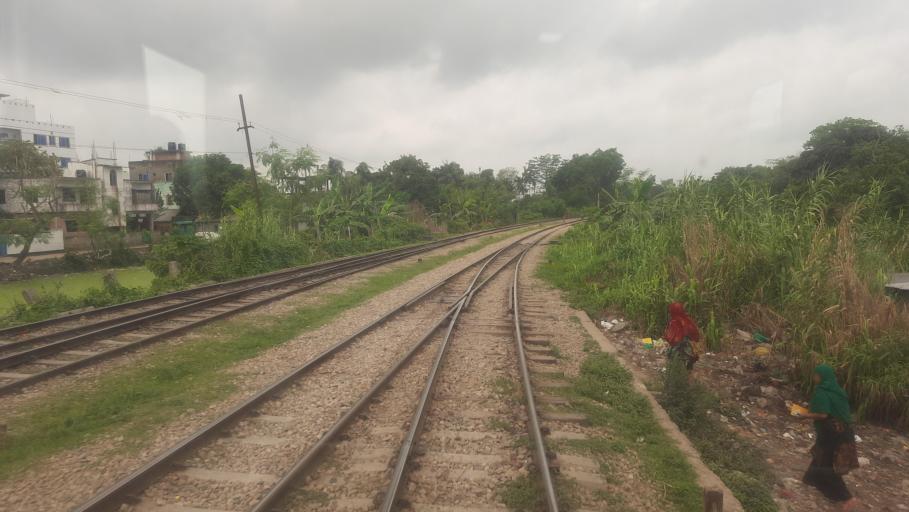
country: BD
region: Dhaka
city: Bhairab Bazar
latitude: 23.9655
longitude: 91.1044
